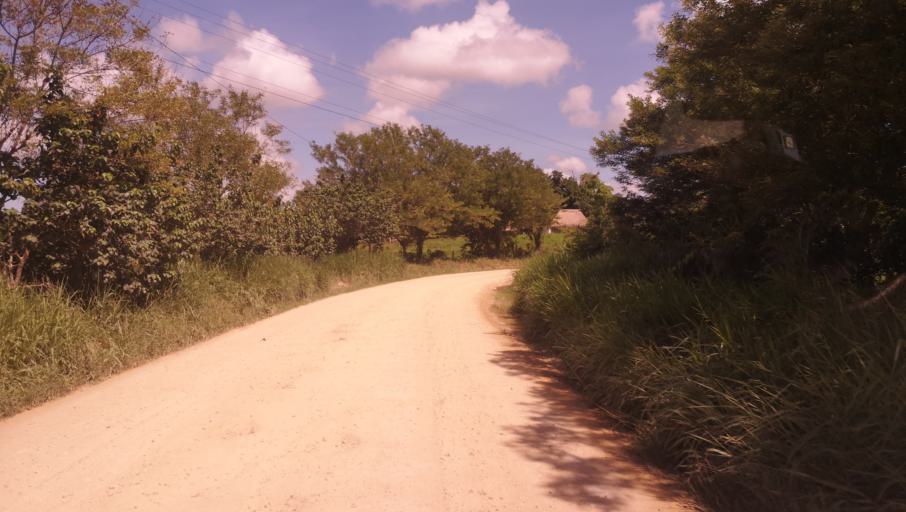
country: GT
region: Peten
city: Melchor de Mencos
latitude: 17.0167
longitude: -89.2443
